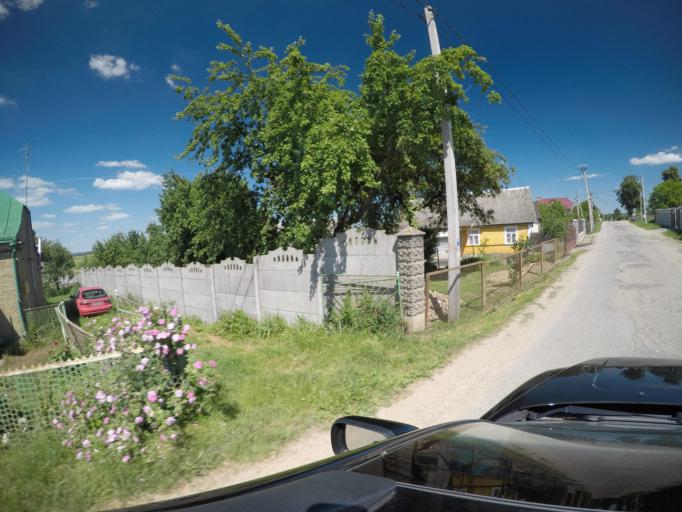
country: BY
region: Grodnenskaya
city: Hrodna
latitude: 53.7239
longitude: 23.8484
